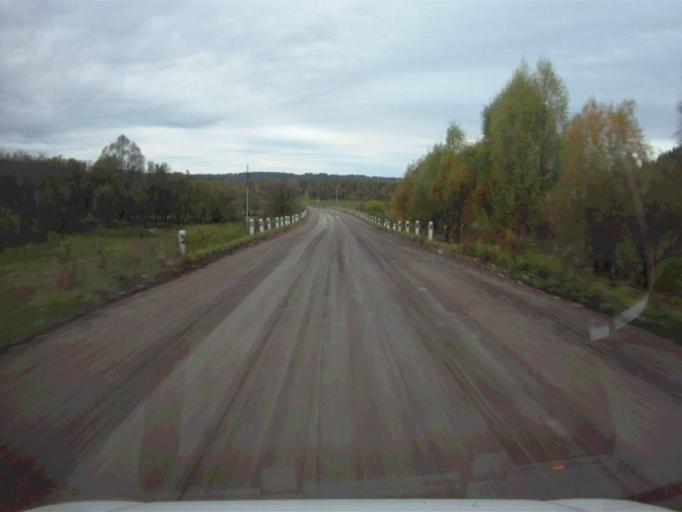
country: RU
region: Chelyabinsk
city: Nyazepetrovsk
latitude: 56.1246
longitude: 59.3546
